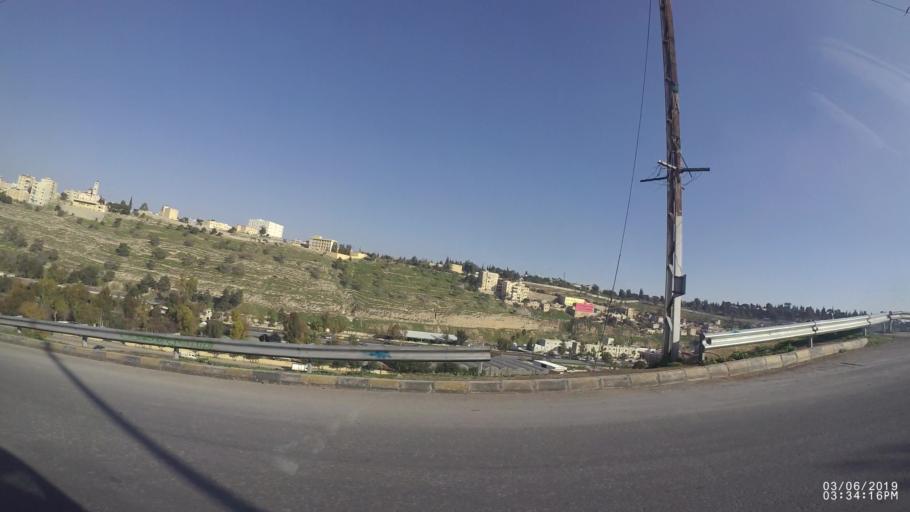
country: JO
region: Amman
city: Amman
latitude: 31.9751
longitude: 35.9694
